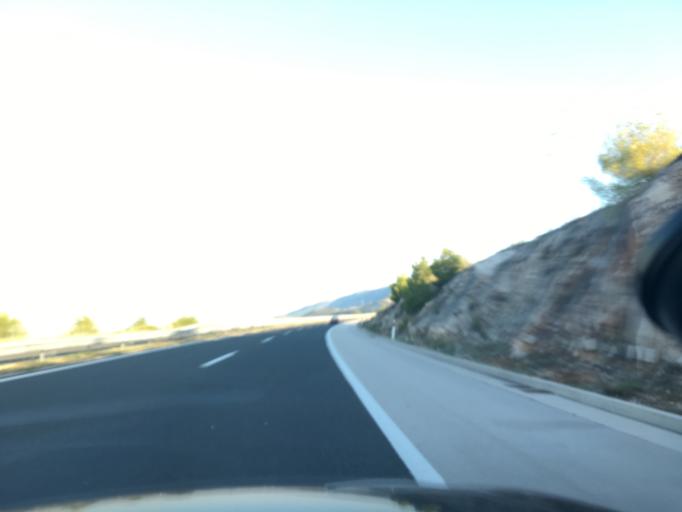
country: HR
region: Sibensko-Kniniska
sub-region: Grad Sibenik
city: Brodarica
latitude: 43.7107
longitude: 15.9911
